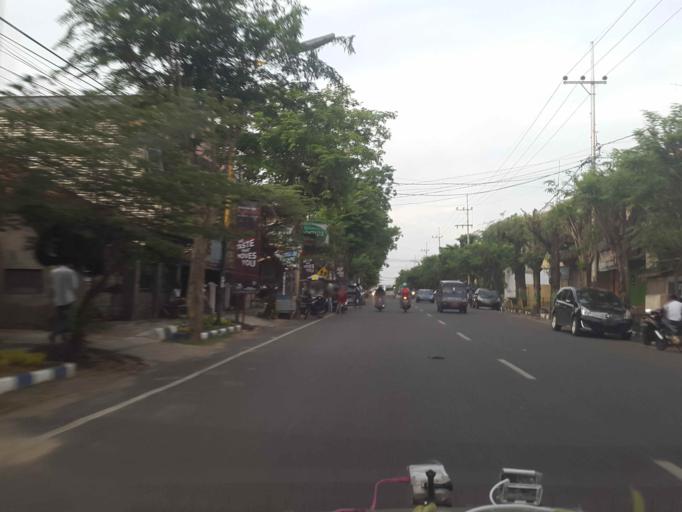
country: ID
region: East Java
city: Sumenep
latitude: -7.0211
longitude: 113.8570
